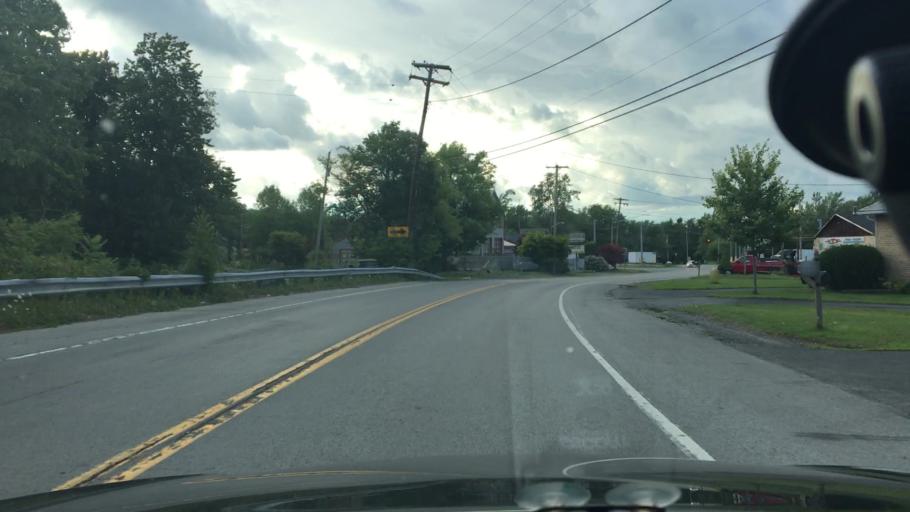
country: US
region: New York
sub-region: Erie County
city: Depew
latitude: 42.8337
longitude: -78.7106
